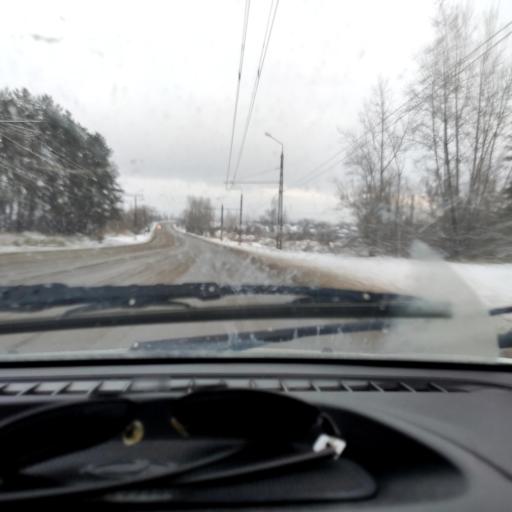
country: RU
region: Samara
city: Zhigulevsk
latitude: 53.4944
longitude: 49.5050
